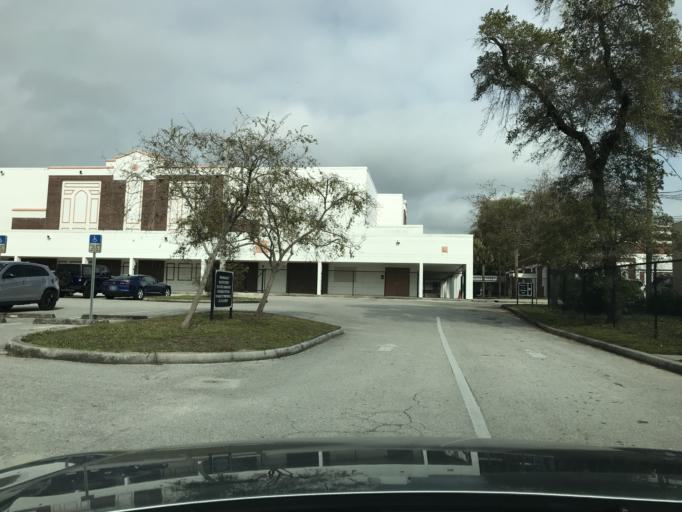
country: US
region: Florida
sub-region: Hillsborough County
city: Tampa
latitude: 27.9871
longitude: -82.4564
